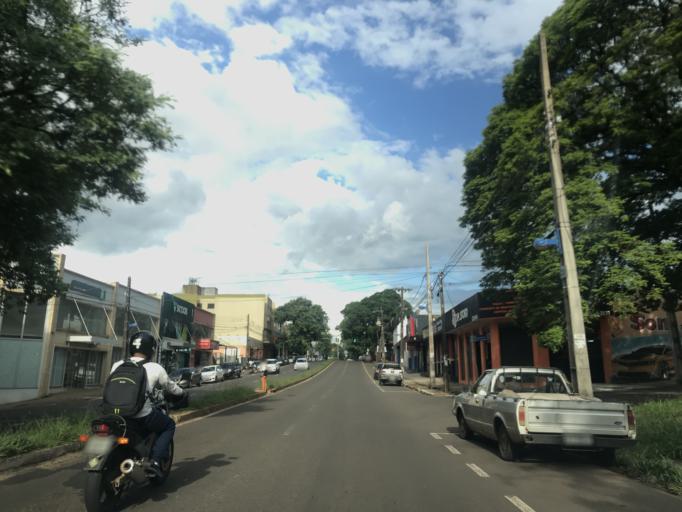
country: BR
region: Parana
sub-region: Maringa
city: Maringa
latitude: -23.4244
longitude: -51.9592
